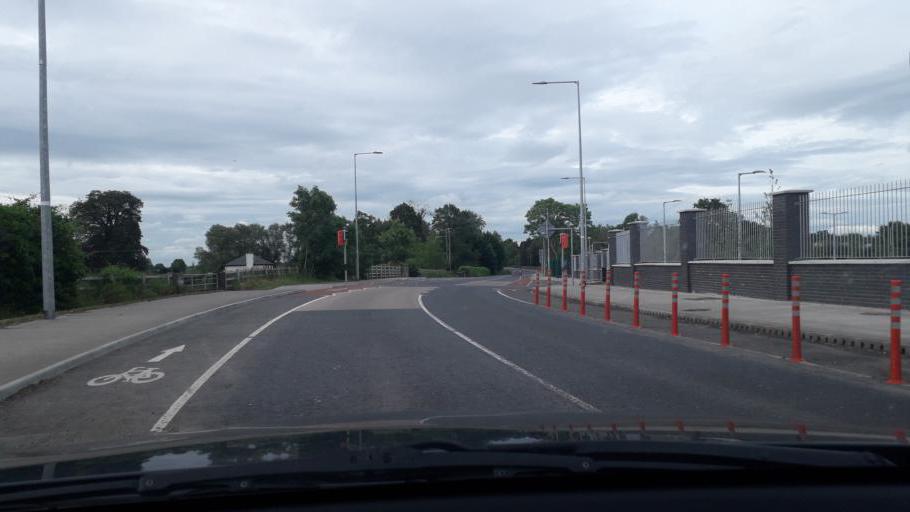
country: IE
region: Leinster
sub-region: County Carlow
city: Carlow
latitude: 52.8186
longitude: -6.9456
